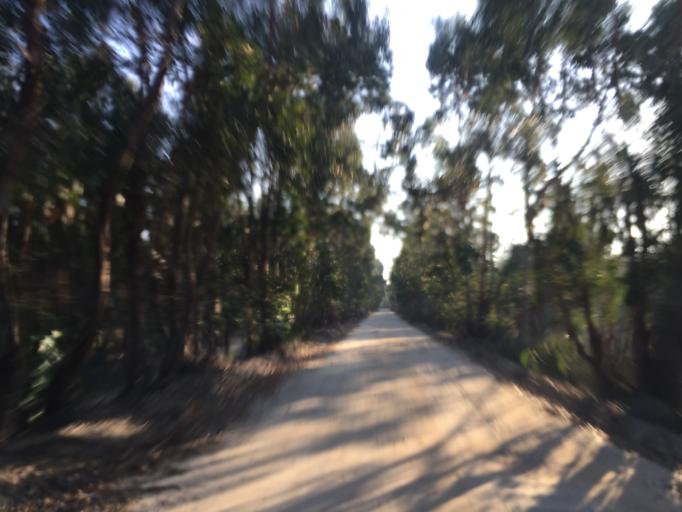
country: PT
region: Portalegre
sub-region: Ponte de Sor
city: Santo Andre
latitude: 39.1435
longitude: -8.3116
